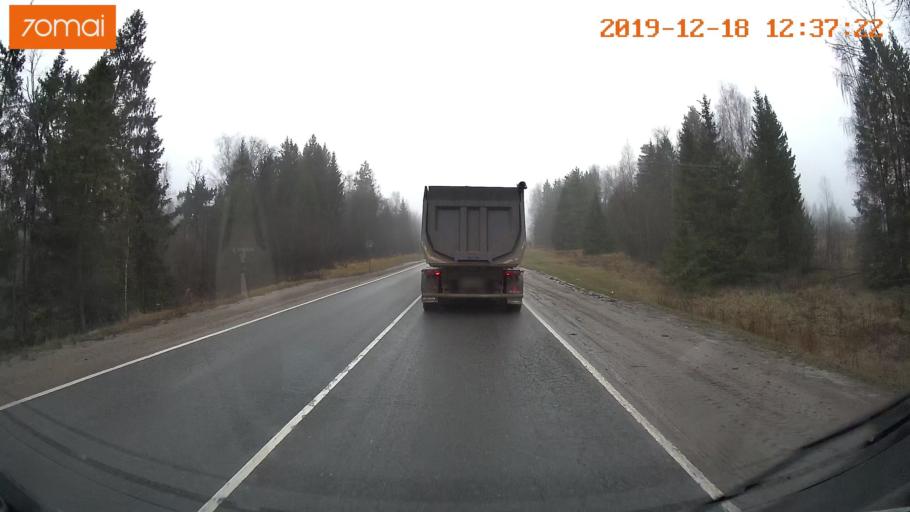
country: RU
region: Moskovskaya
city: Vysokovsk
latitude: 56.1445
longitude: 36.6008
